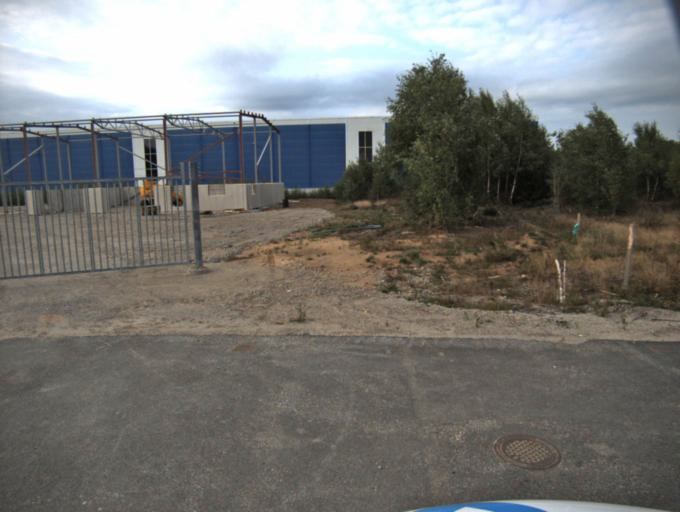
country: SE
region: Vaestra Goetaland
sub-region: Ulricehamns Kommun
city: Ulricehamn
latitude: 57.8351
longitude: 13.4254
